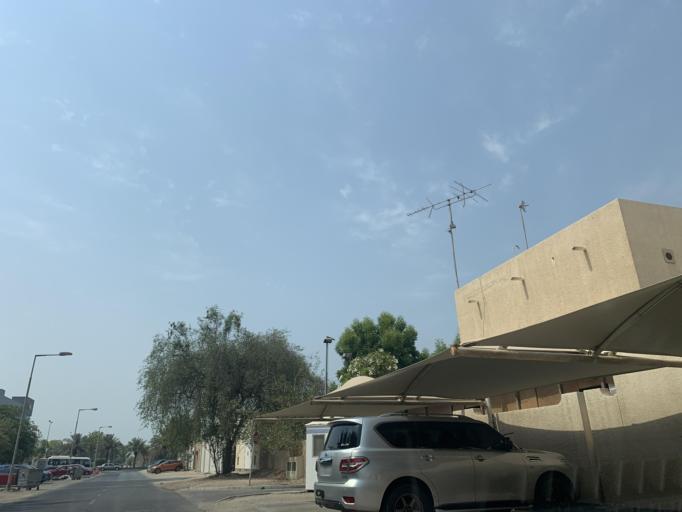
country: BH
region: Manama
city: Jidd Hafs
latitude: 26.2172
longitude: 50.4871
